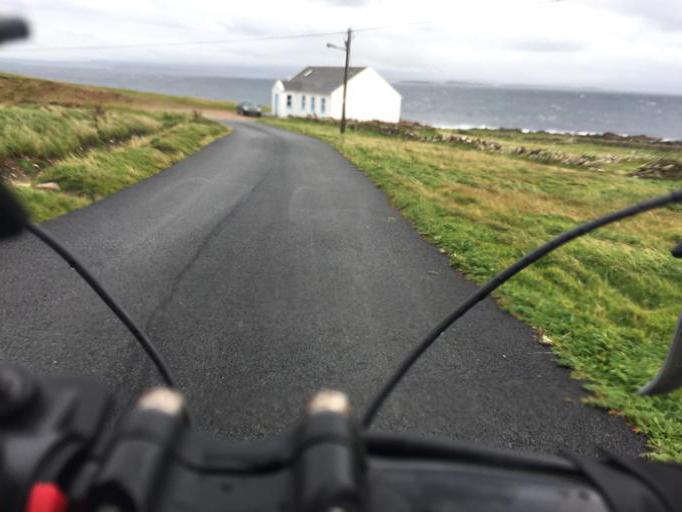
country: IE
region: Ulster
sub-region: County Donegal
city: Derrybeg
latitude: 55.2558
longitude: -8.1962
